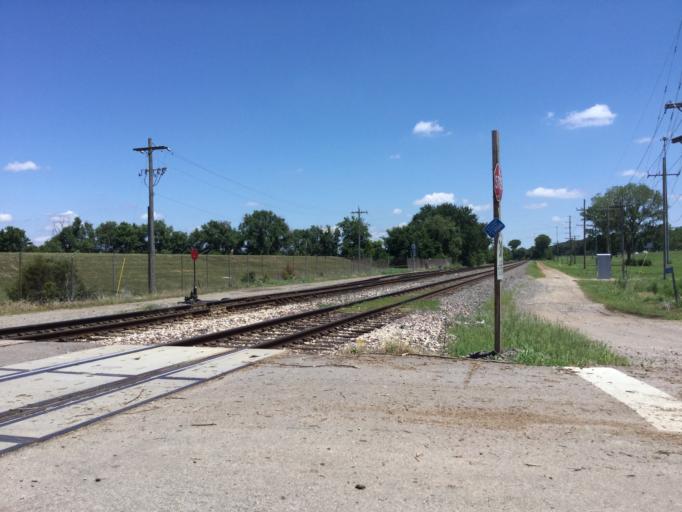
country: US
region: Kansas
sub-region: Shawnee County
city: Topeka
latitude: 39.0700
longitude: -95.7014
